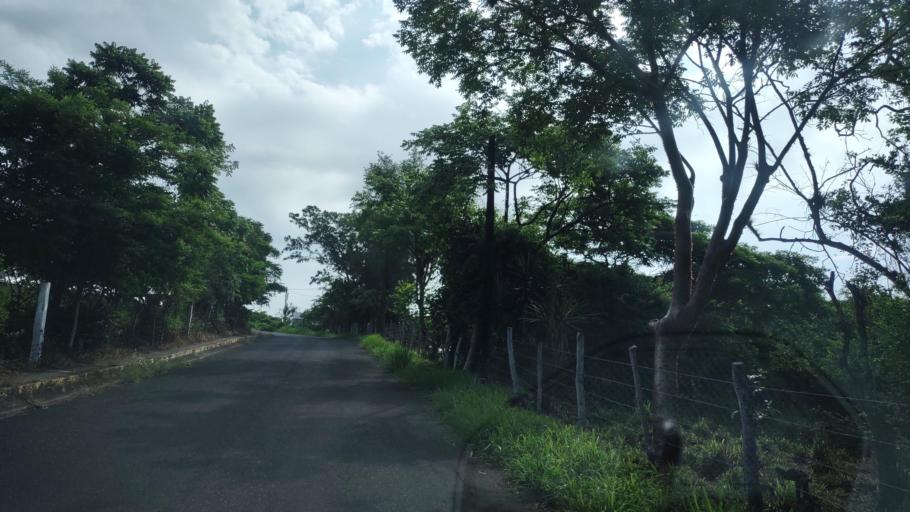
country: MX
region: Veracruz
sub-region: Coatepec
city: Bella Esperanza
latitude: 19.4500
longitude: -96.8276
